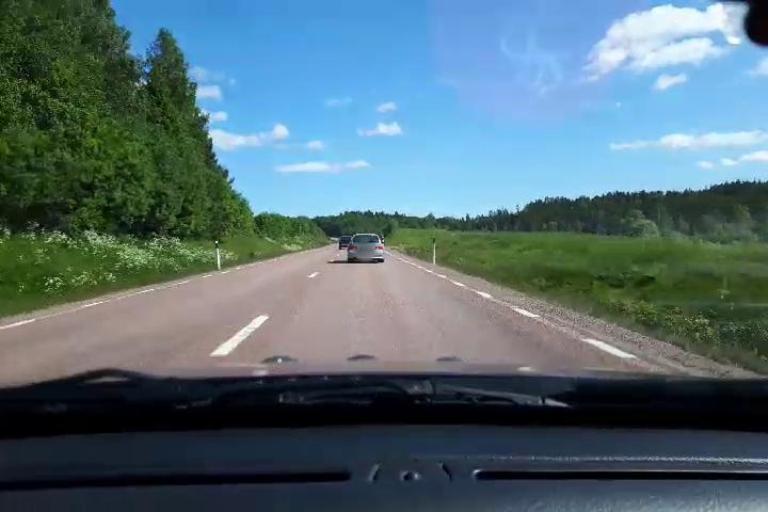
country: SE
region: Gaevleborg
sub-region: Hudiksvalls Kommun
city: Sorforsa
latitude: 61.7445
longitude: 16.8509
